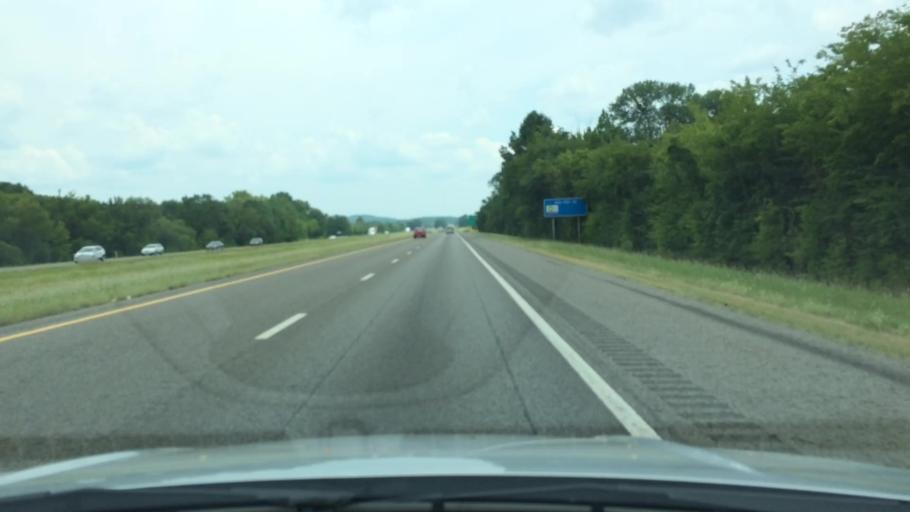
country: US
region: Tennessee
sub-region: Marshall County
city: Cornersville
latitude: 35.4301
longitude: -86.8796
